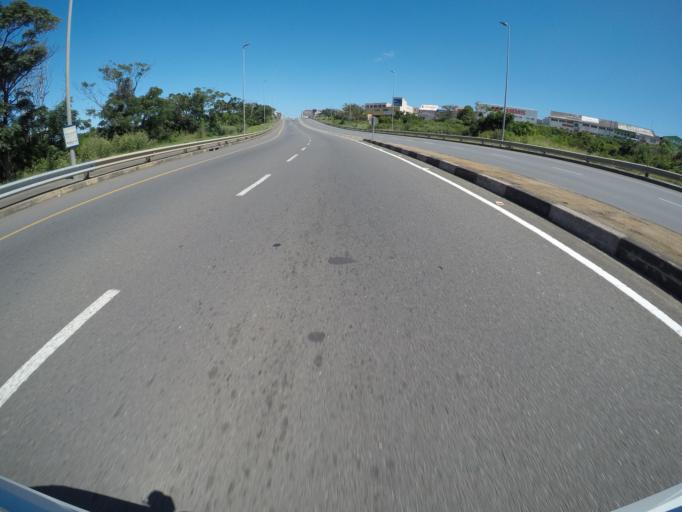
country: ZA
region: Eastern Cape
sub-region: Buffalo City Metropolitan Municipality
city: East London
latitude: -33.0047
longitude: 27.9128
